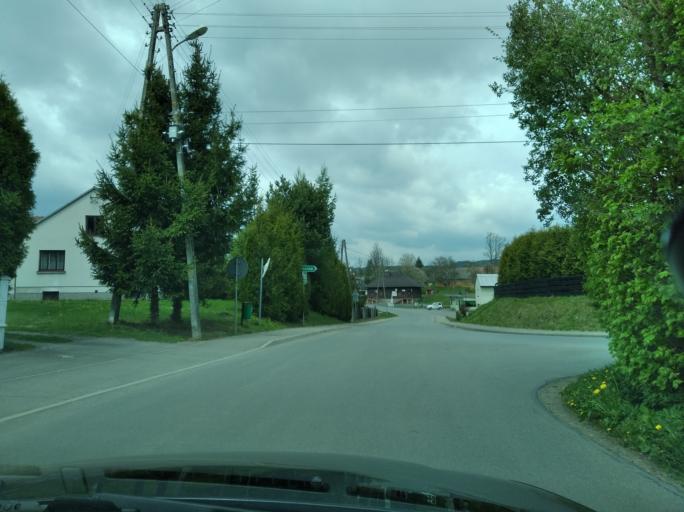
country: PL
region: Subcarpathian Voivodeship
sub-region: Powiat brzozowski
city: Jablonica Polska
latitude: 49.6966
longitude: 21.9016
